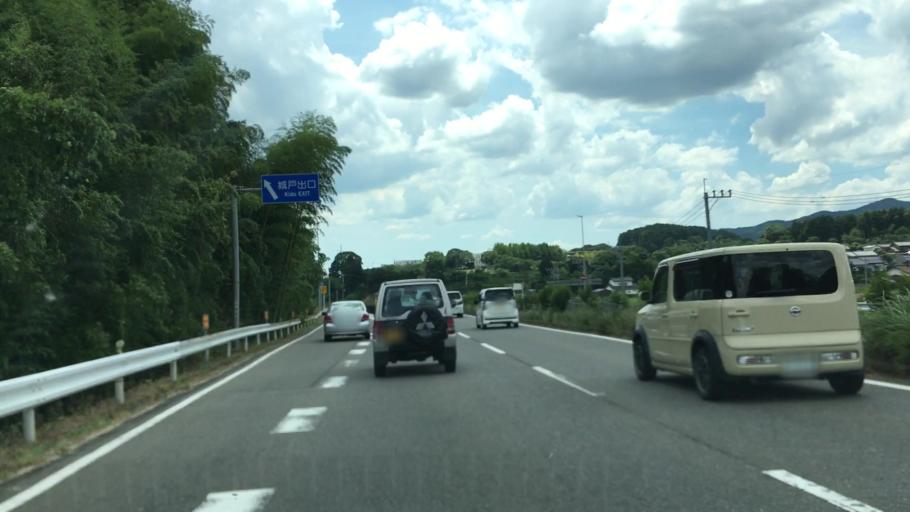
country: JP
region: Fukuoka
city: Chikushino-shi
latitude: 33.4357
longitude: 130.5249
